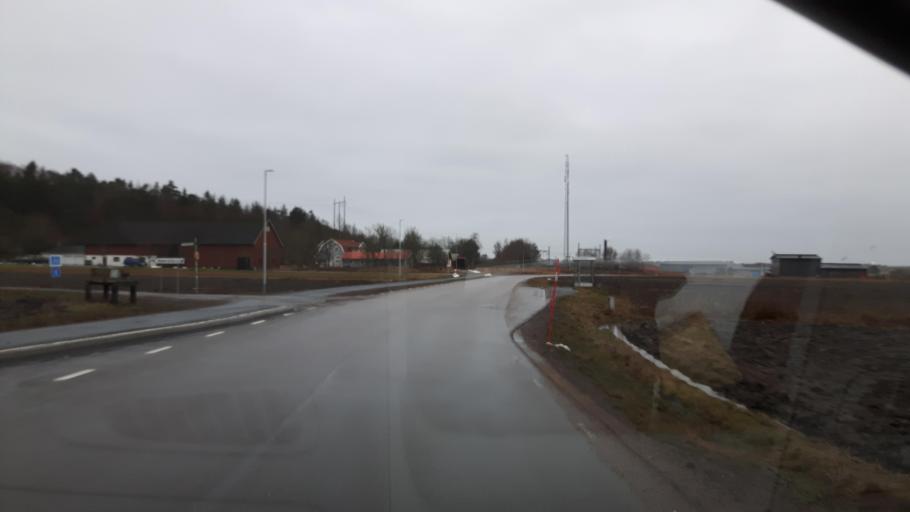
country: SE
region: Halland
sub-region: Kungsbacka Kommun
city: Frillesas
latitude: 57.3601
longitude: 12.1282
